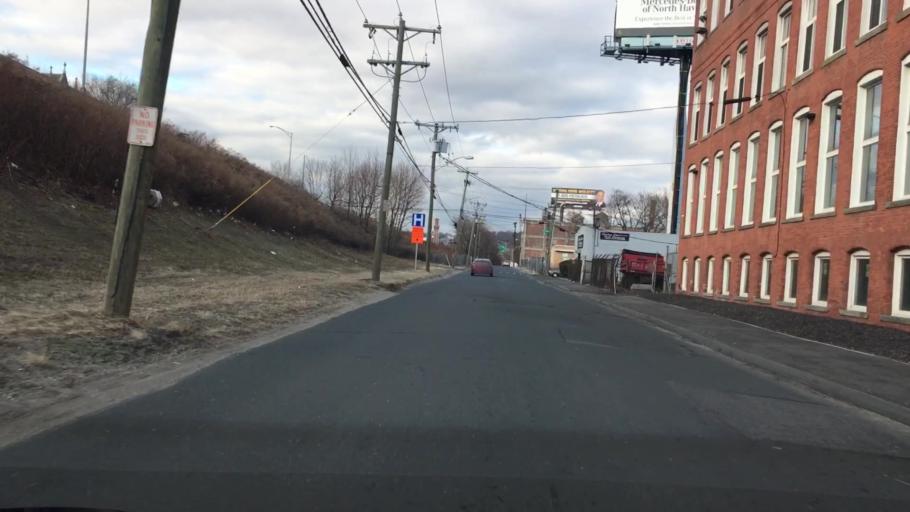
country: US
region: Connecticut
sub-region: New Haven County
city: Waterbury
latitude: 41.5413
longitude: -73.0440
